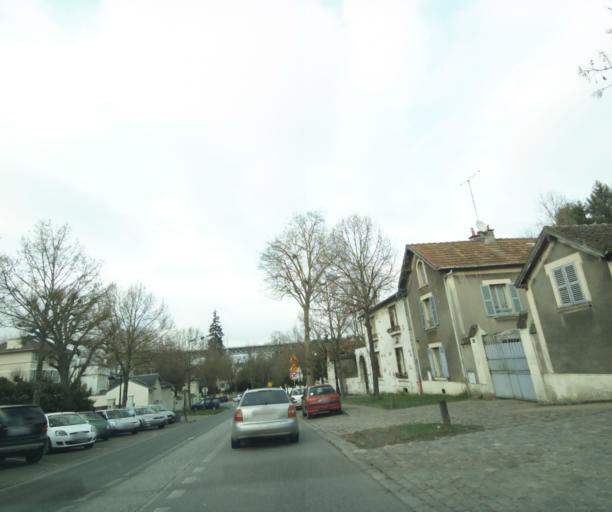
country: FR
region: Ile-de-France
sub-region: Departement des Yvelines
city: Louveciennes
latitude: 48.8687
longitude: 2.1025
